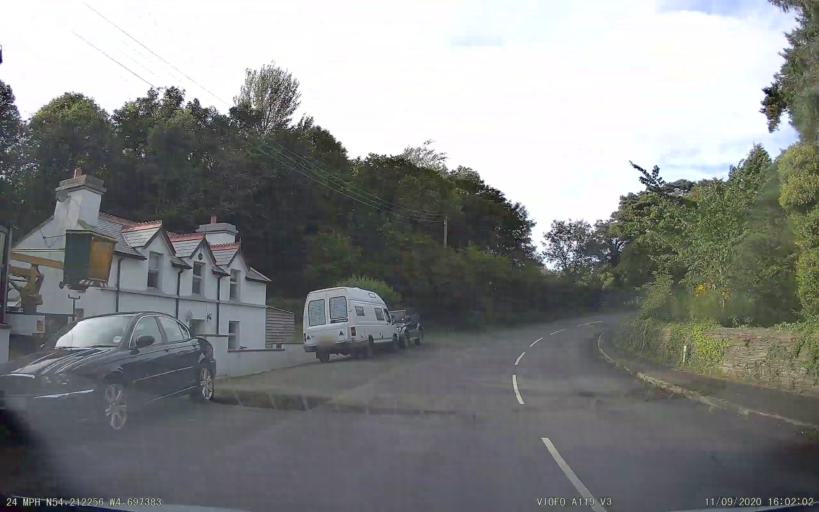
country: IM
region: Port Erin
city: Port Erin
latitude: 54.2123
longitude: -4.6974
